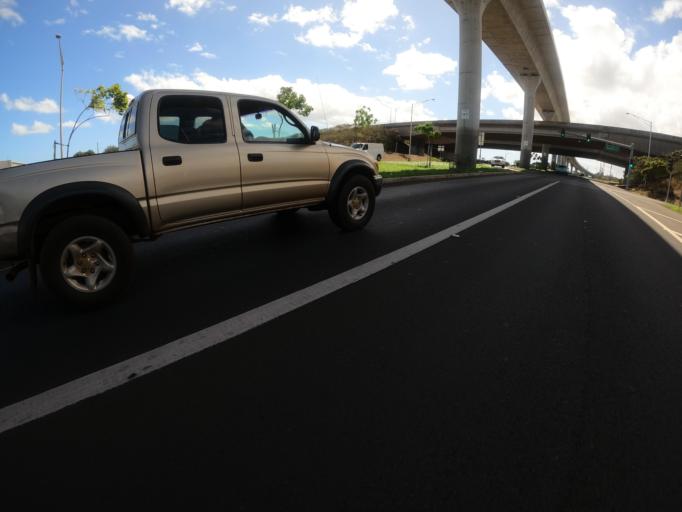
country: US
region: Hawaii
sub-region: Honolulu County
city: Royal Kunia
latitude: 21.3766
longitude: -158.0261
